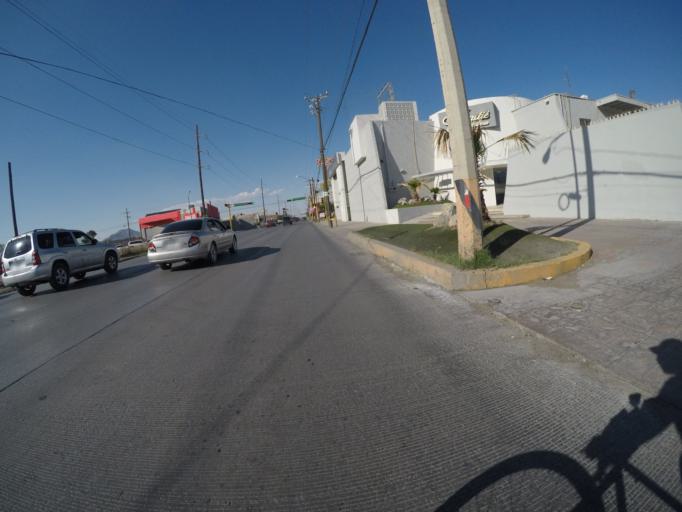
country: MX
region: Chihuahua
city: Ciudad Juarez
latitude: 31.7186
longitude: -106.4439
